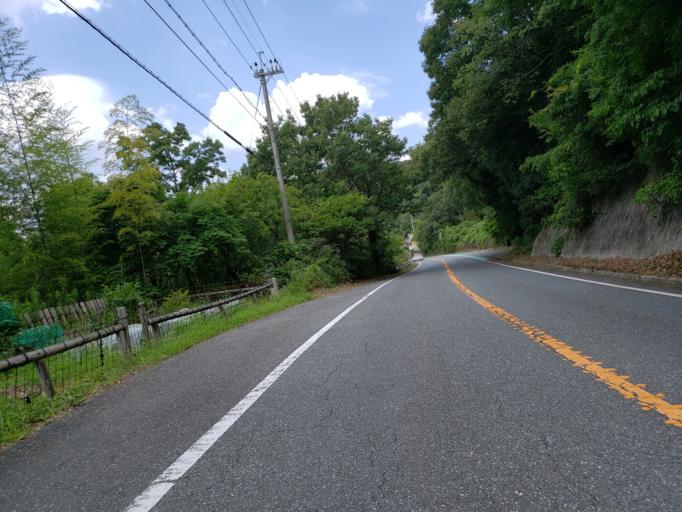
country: JP
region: Hyogo
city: Aioi
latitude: 34.7669
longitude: 134.4743
